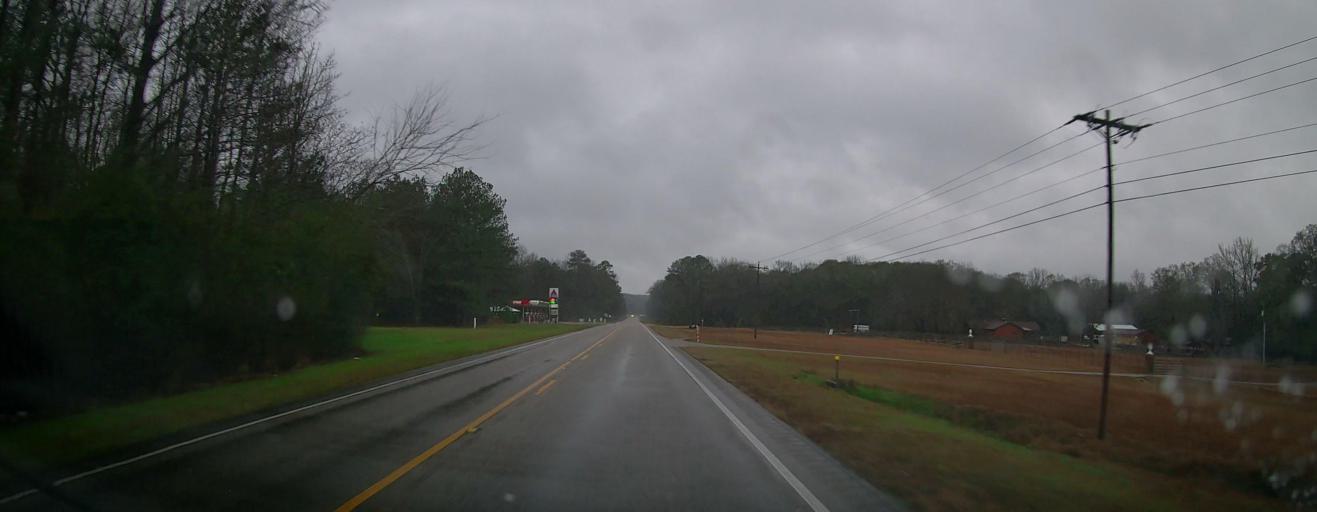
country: US
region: Alabama
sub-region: Autauga County
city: Prattville
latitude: 32.4905
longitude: -86.5480
